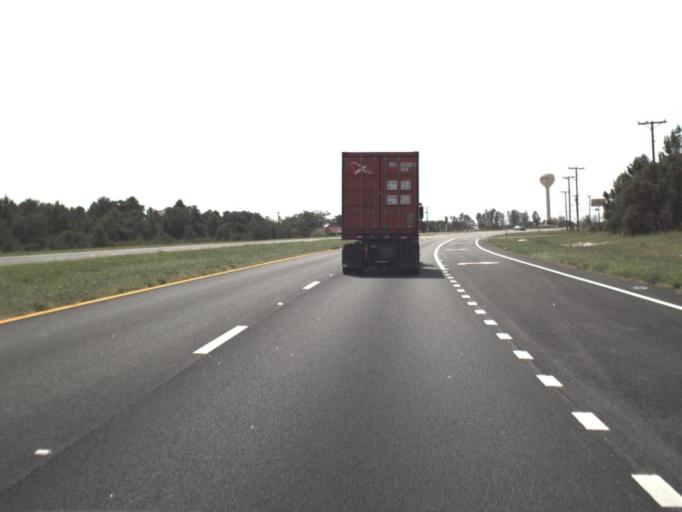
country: US
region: Florida
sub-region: Polk County
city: Frostproof
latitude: 27.7155
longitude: -81.5611
